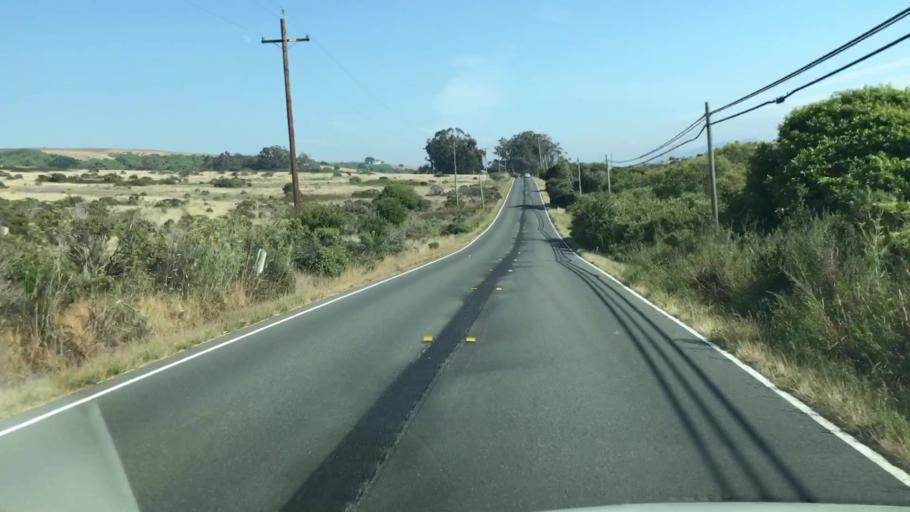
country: US
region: California
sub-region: Marin County
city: Inverness
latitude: 38.1123
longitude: -122.8490
